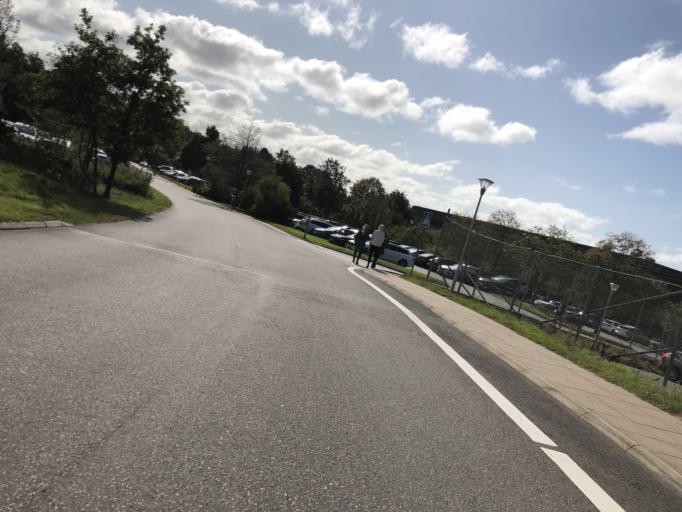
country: SE
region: Vaestra Goetaland
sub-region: Goteborg
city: Majorna
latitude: 57.7269
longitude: 11.8527
